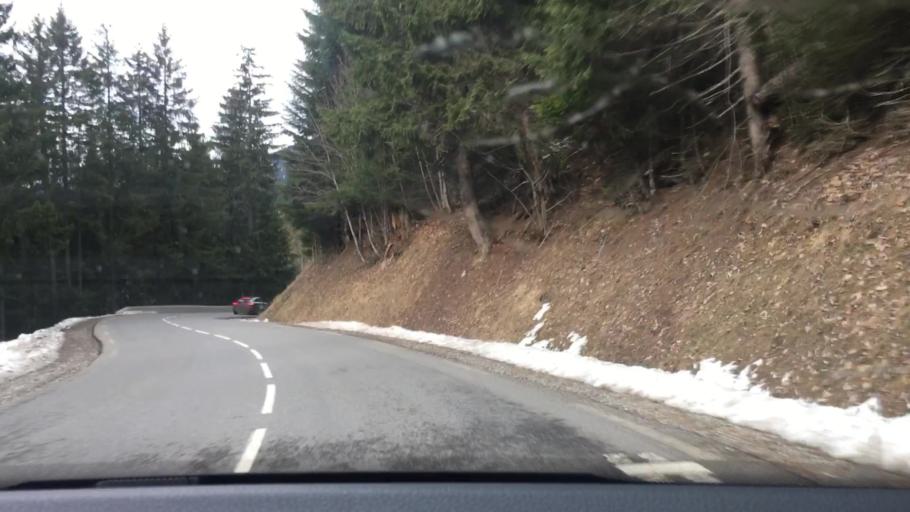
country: FR
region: Rhone-Alpes
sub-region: Departement de la Haute-Savoie
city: Chatel
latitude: 46.2547
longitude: 6.8457
